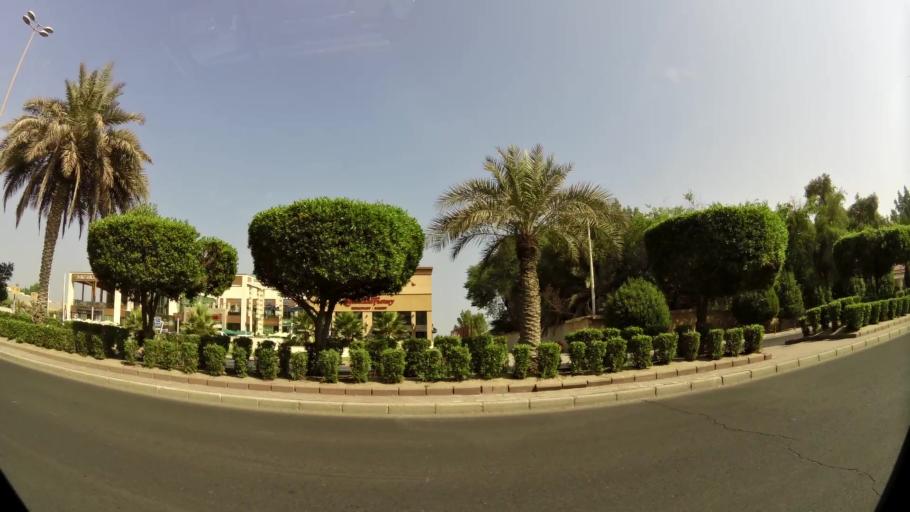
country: KW
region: Al Ahmadi
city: Al Mahbulah
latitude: 29.1474
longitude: 48.1276
